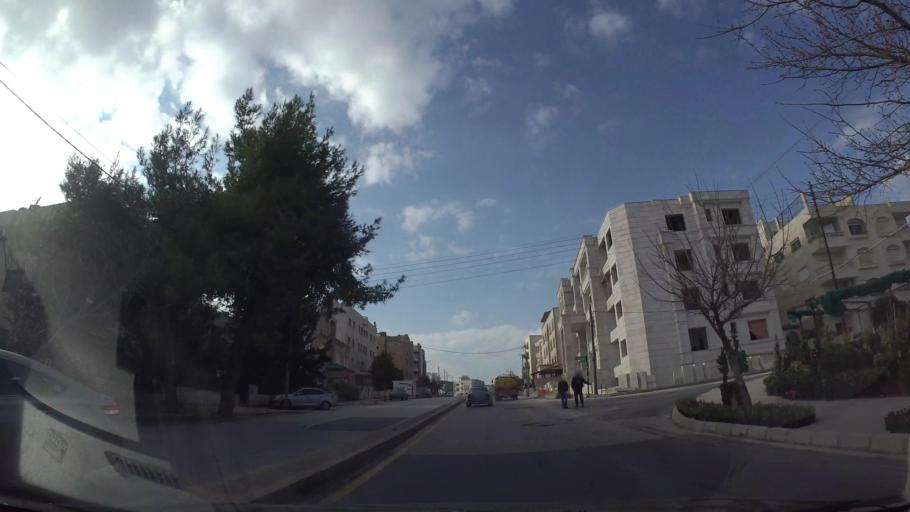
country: JO
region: Amman
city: Al Jubayhah
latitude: 31.9782
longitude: 35.8857
